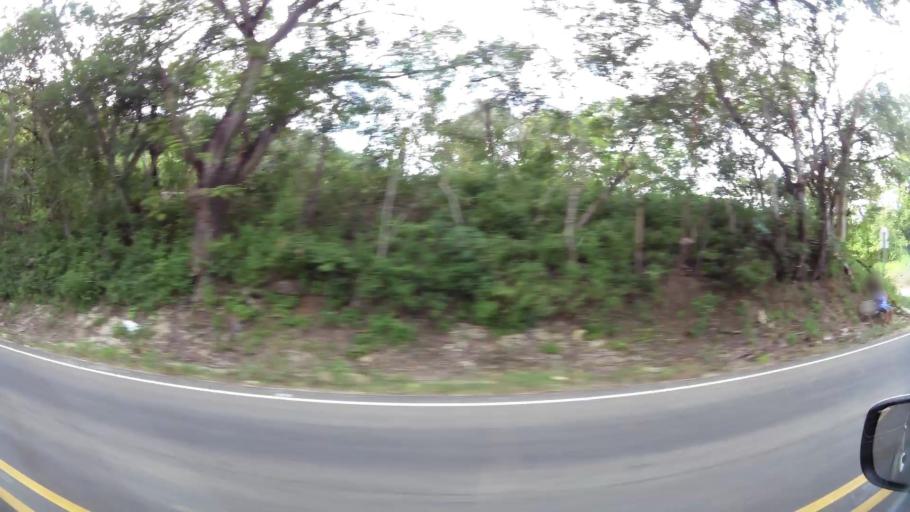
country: CR
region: Guanacaste
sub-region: Canton de Nicoya
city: Nicoya
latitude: 10.1592
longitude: -85.3059
